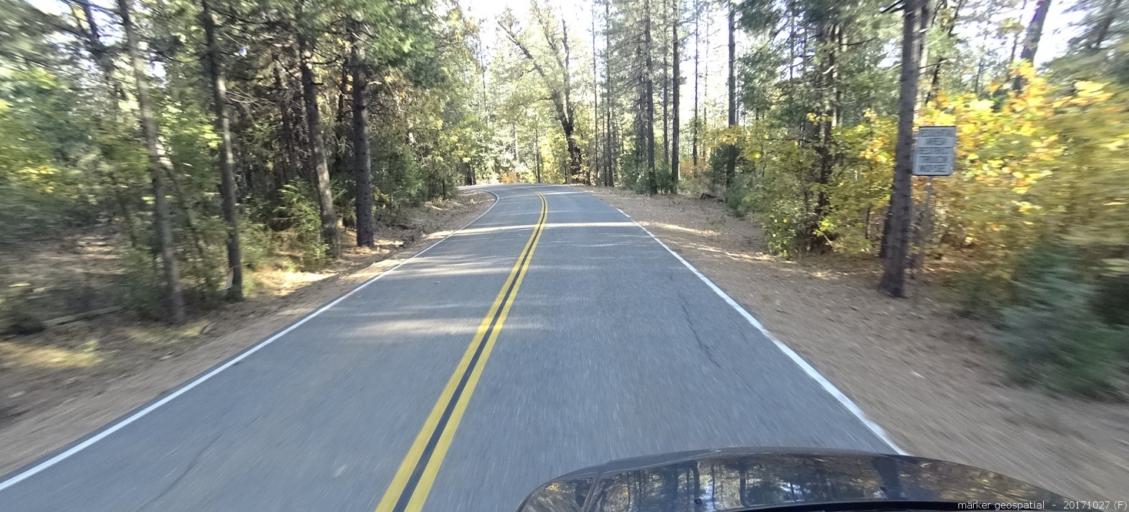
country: US
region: California
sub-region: Shasta County
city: Burney
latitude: 40.9957
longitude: -121.9201
